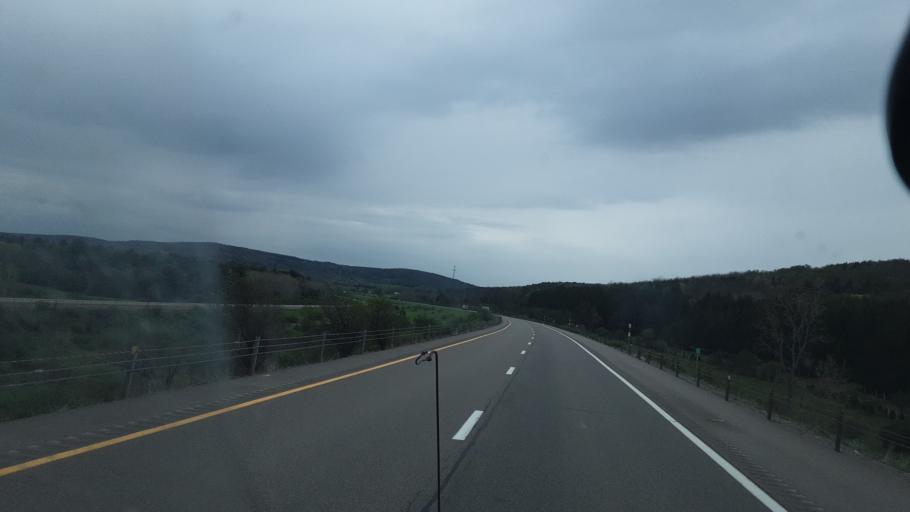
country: US
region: New York
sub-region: Allegany County
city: Belmont
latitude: 42.2927
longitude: -77.9775
